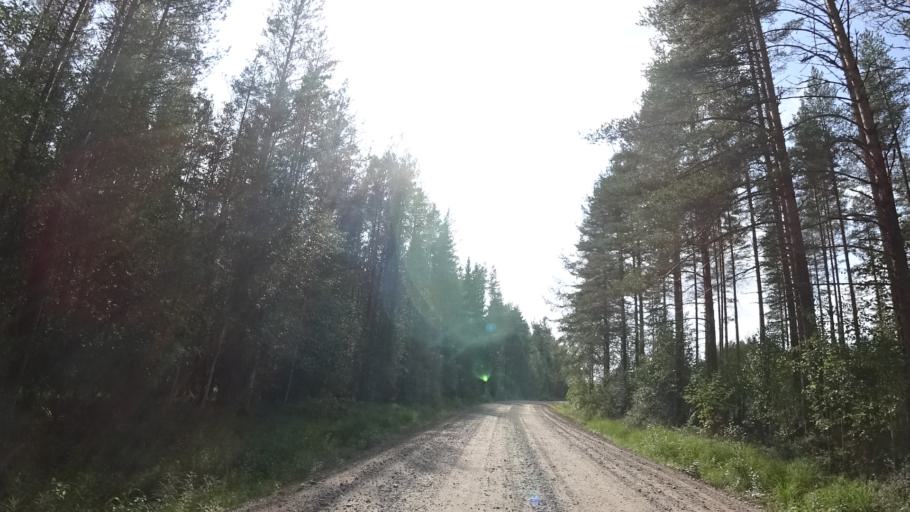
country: FI
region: North Karelia
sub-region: Pielisen Karjala
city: Lieksa
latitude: 63.5679
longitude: 30.0945
